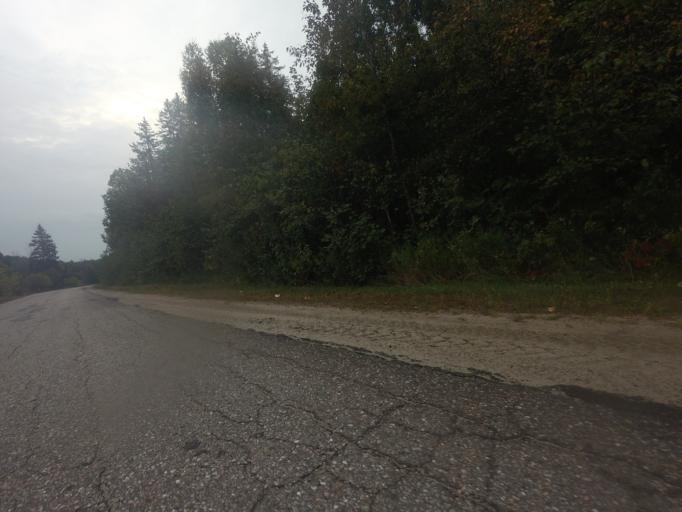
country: CA
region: Quebec
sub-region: Outaouais
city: Maniwaki
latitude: 46.0891
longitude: -76.0345
